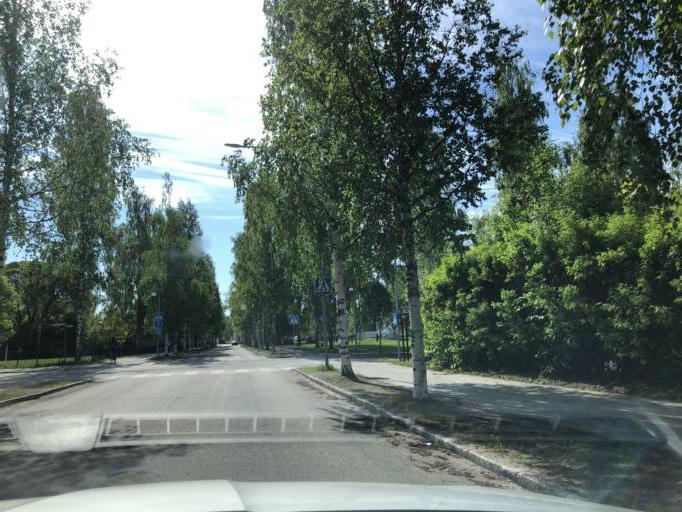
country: SE
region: Norrbotten
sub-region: Pitea Kommun
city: Pitea
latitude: 65.3194
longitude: 21.4824
